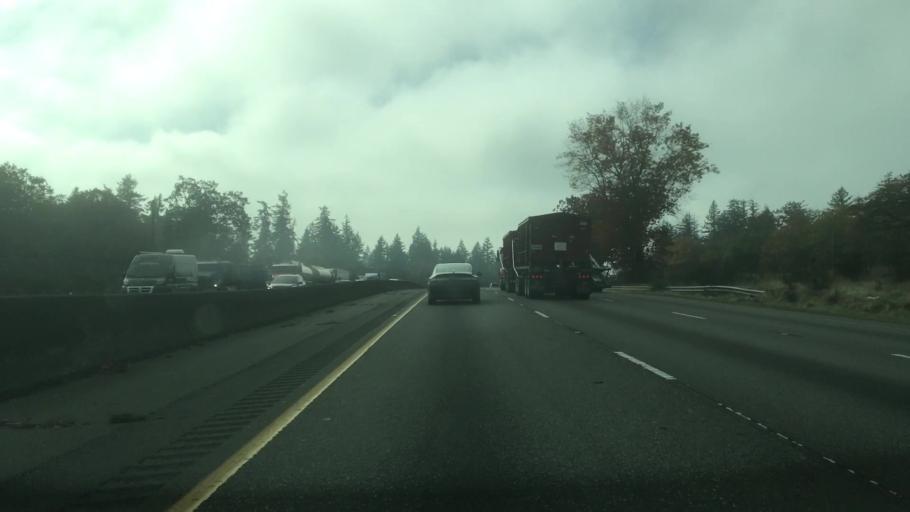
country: US
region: Washington
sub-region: Pierce County
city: Fort Lewis
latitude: 47.1123
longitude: -122.5679
